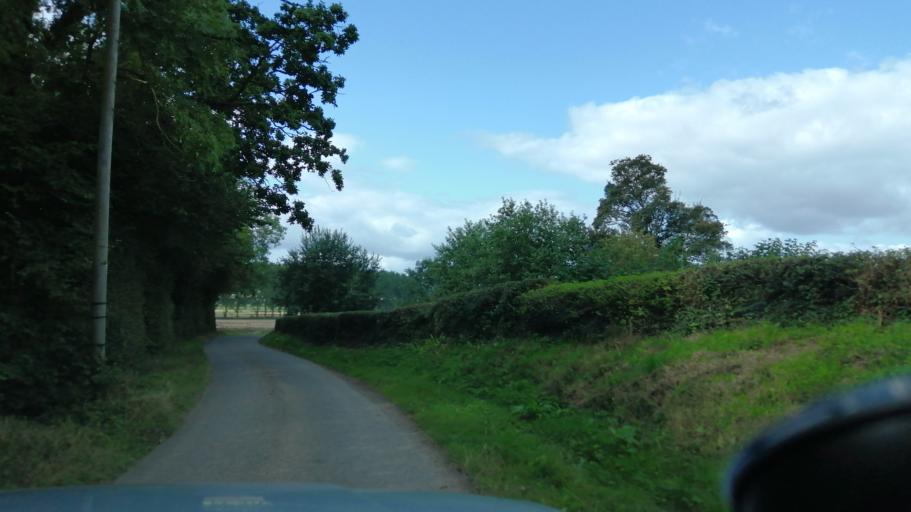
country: GB
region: England
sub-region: Herefordshire
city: Kinnersley
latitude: 52.1223
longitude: -2.9157
